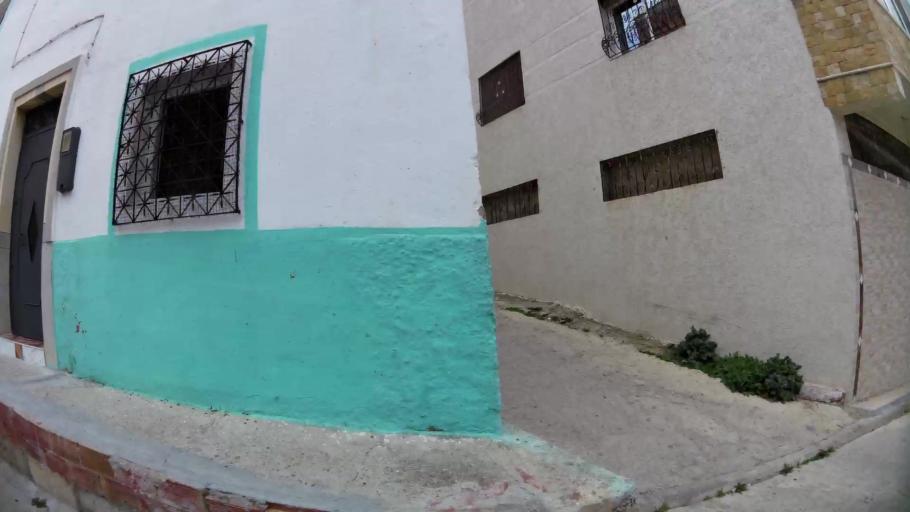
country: MA
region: Tanger-Tetouan
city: Tetouan
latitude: 35.5698
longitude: -5.3920
